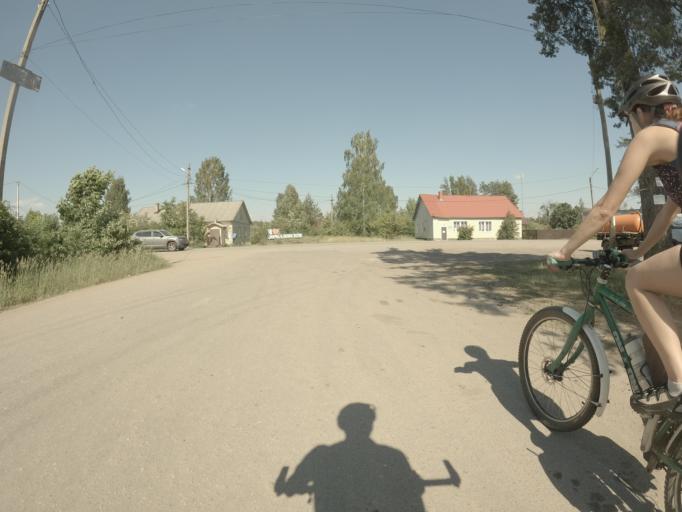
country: RU
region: Leningrad
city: Yakovlevo
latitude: 60.4688
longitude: 29.2861
